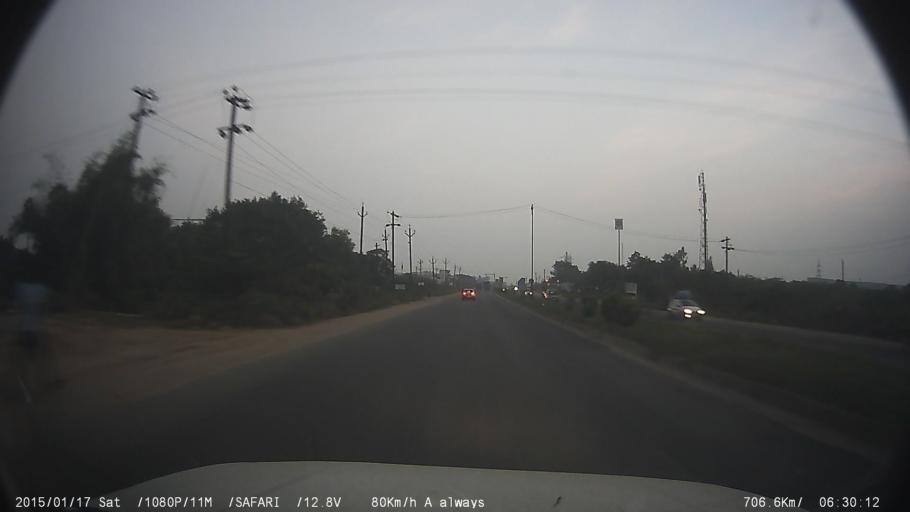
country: IN
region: Tamil Nadu
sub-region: Kancheepuram
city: Sriperumbudur
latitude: 12.9483
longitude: 79.9251
